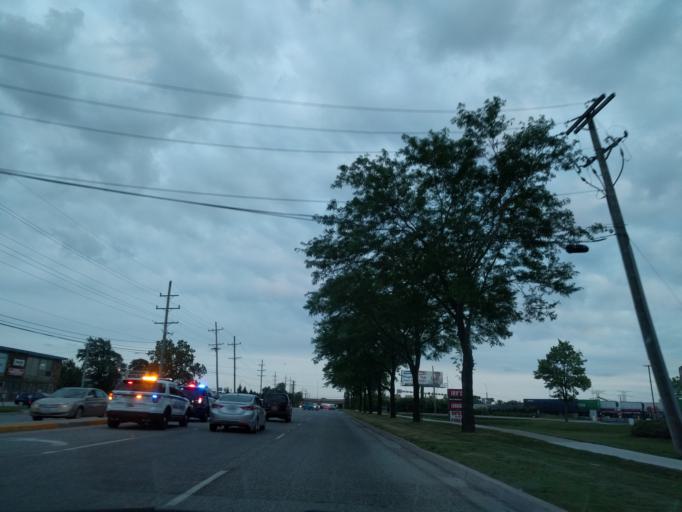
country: US
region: Illinois
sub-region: Cook County
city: Elk Grove Village
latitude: 42.0292
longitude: -87.9601
